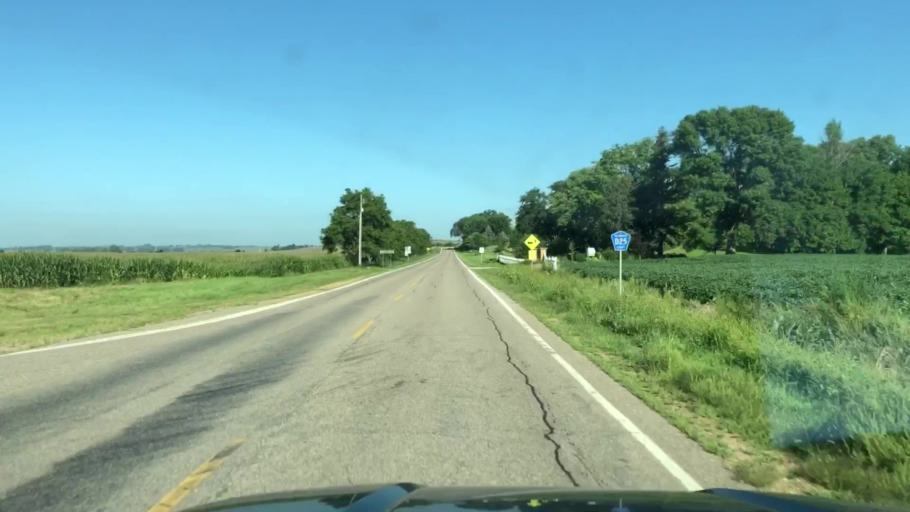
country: US
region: Iowa
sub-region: Woodbury County
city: Sergeant Bluff
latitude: 42.4027
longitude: -96.2444
